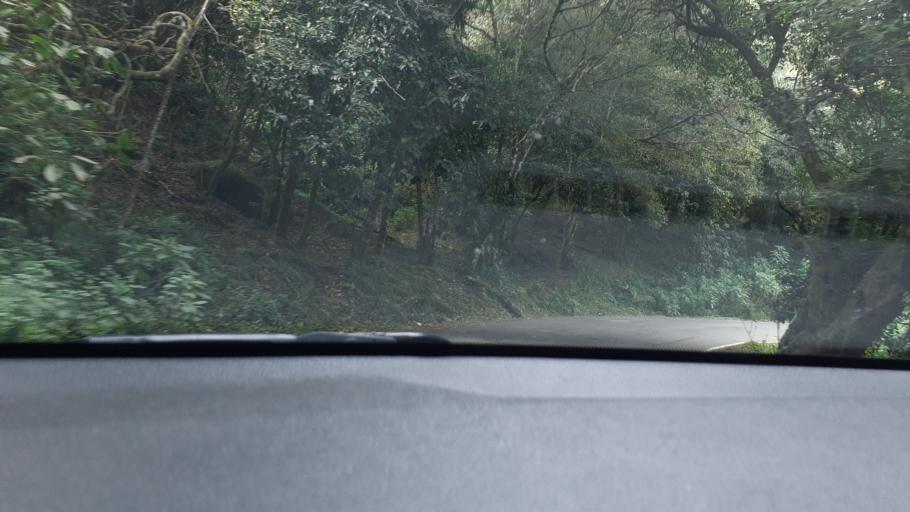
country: IN
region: Tamil Nadu
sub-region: Dindigul
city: Kodaikanal
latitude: 10.2447
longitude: 77.4189
